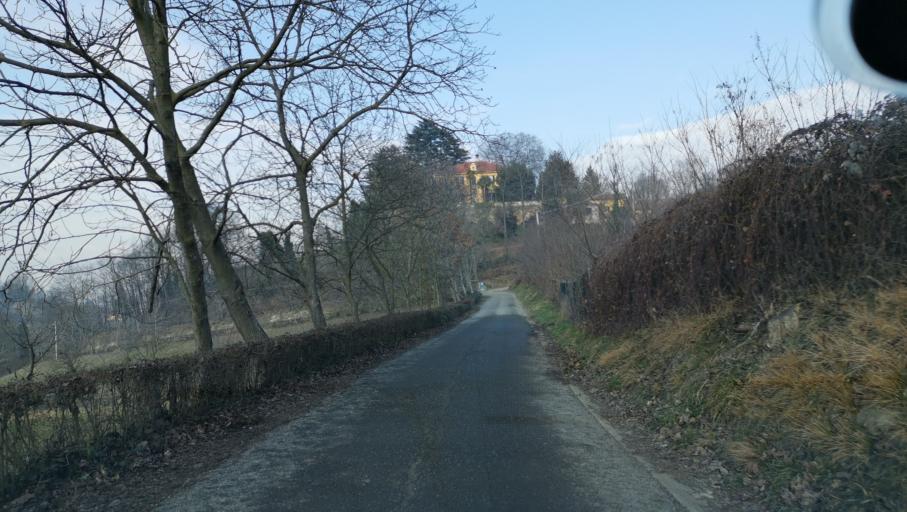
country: IT
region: Piedmont
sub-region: Provincia di Torino
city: Gassino Torinese
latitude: 45.1176
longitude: 7.8339
